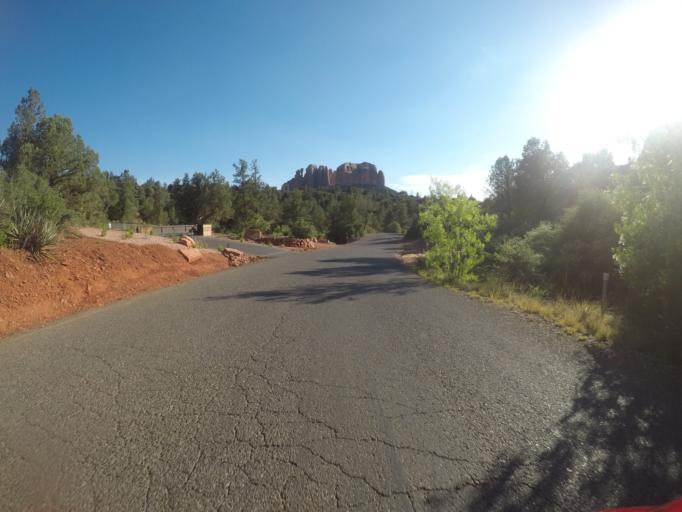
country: US
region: Arizona
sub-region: Yavapai County
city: West Sedona
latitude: 34.8263
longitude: -111.7832
